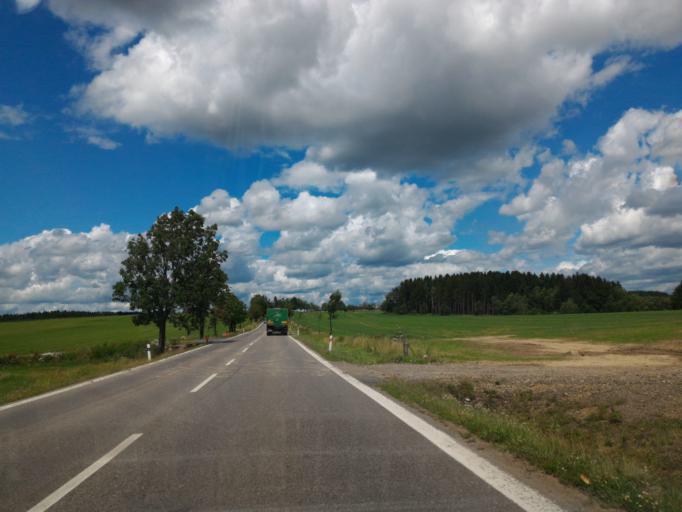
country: CZ
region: Vysocina
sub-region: Okres Zd'ar nad Sazavou
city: Nove Veseli
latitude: 49.5257
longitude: 15.9098
